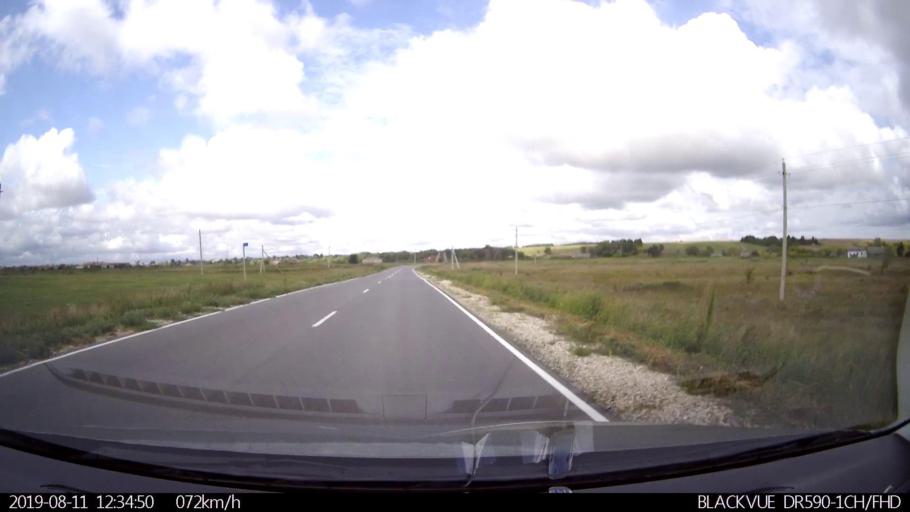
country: RU
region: Ulyanovsk
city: Ignatovka
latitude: 53.8198
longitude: 47.8377
